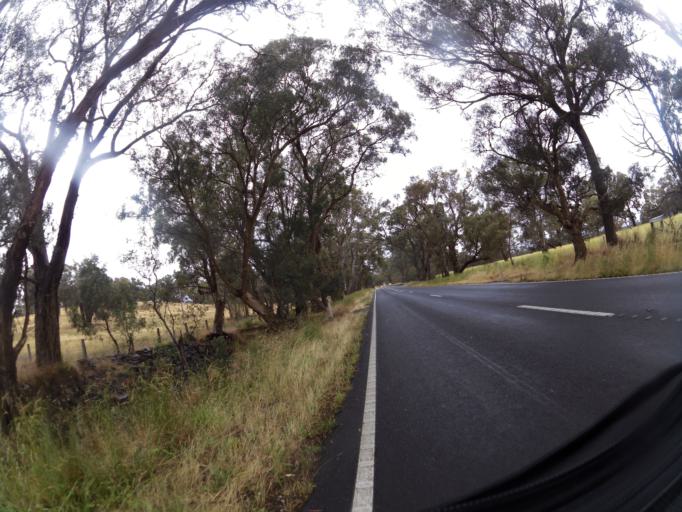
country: AU
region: Victoria
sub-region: Mount Alexander
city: Castlemaine
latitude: -37.0943
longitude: 144.1356
